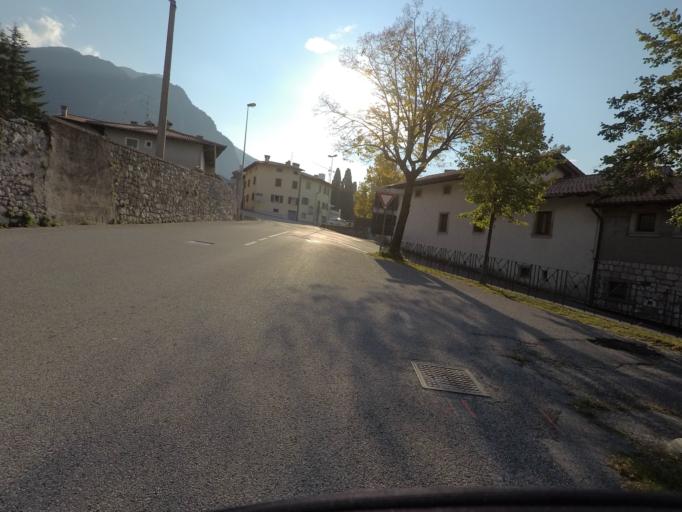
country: IT
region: Friuli Venezia Giulia
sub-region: Provincia di Udine
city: Gemona
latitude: 46.2795
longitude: 13.1343
